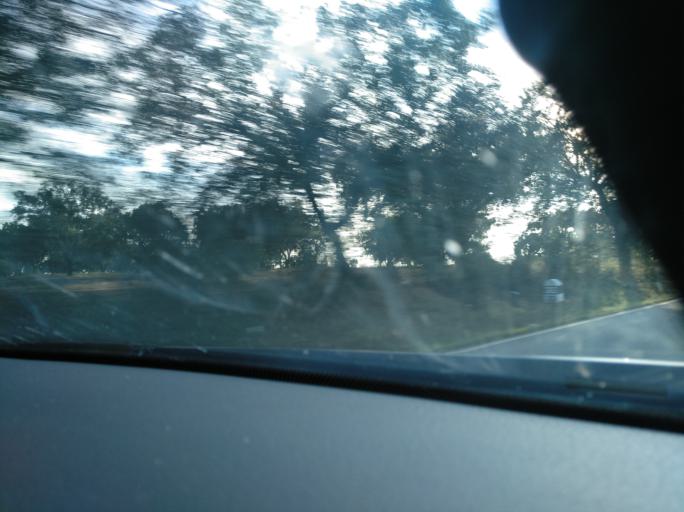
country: PT
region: Portalegre
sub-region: Fronteira
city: Fronteira
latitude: 38.9619
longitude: -7.5991
